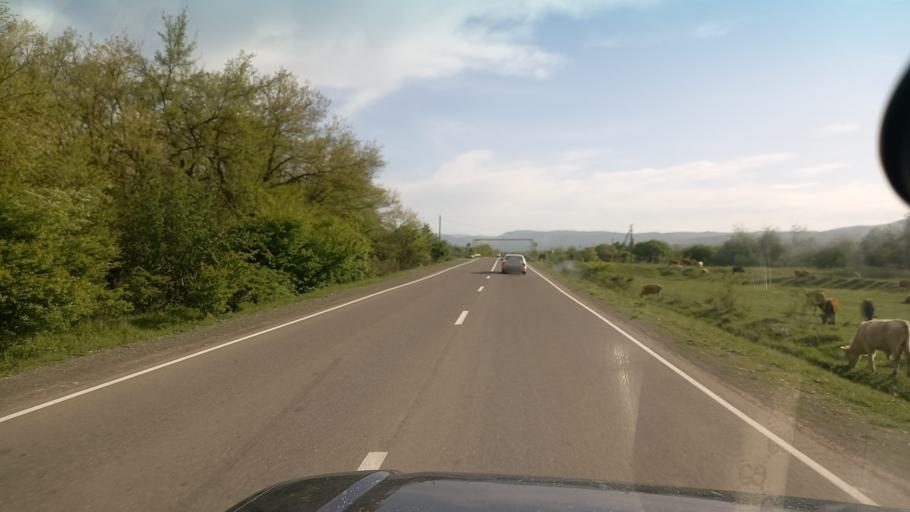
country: RU
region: Ingushetiya
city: Nesterovskaya
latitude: 43.2178
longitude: 45.0272
